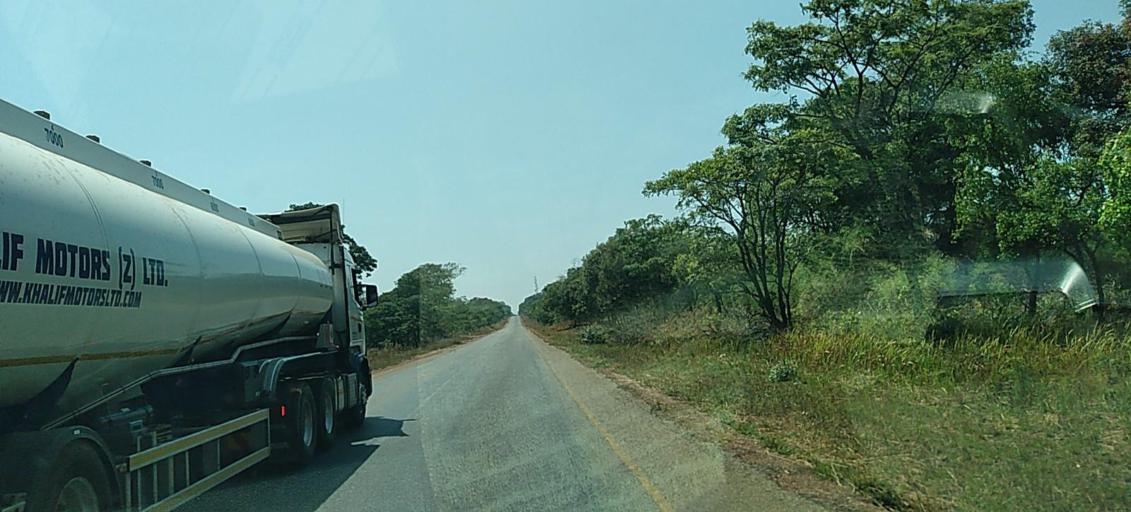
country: ZM
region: North-Western
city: Solwezi
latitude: -12.3629
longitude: 25.9726
